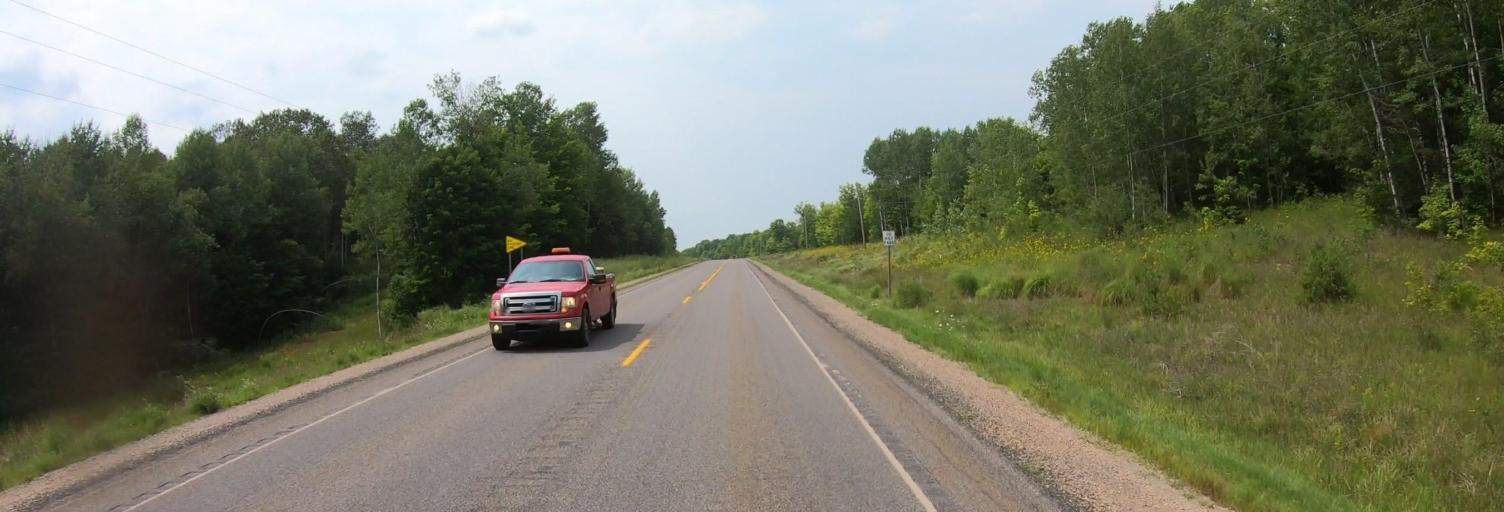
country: US
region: Michigan
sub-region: Alger County
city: Munising
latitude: 46.3322
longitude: -86.8667
